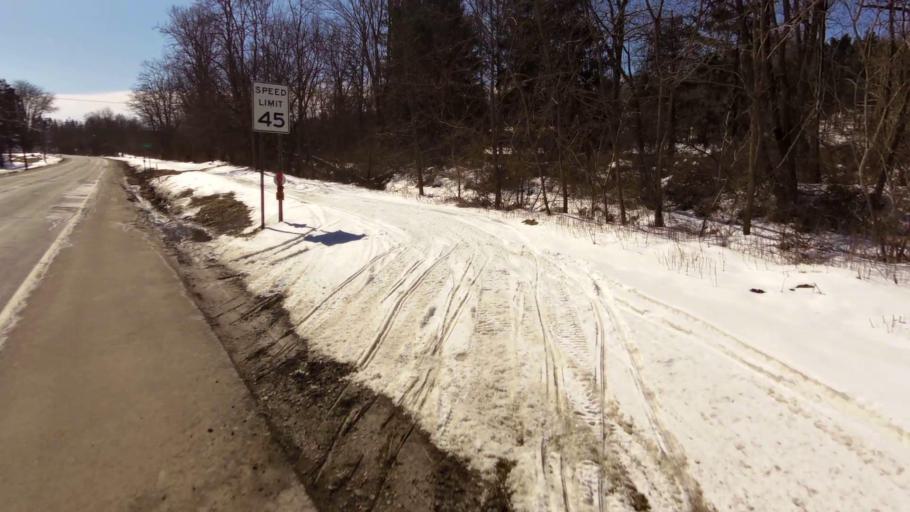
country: US
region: New York
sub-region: Allegany County
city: Houghton
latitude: 42.3703
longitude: -78.1401
